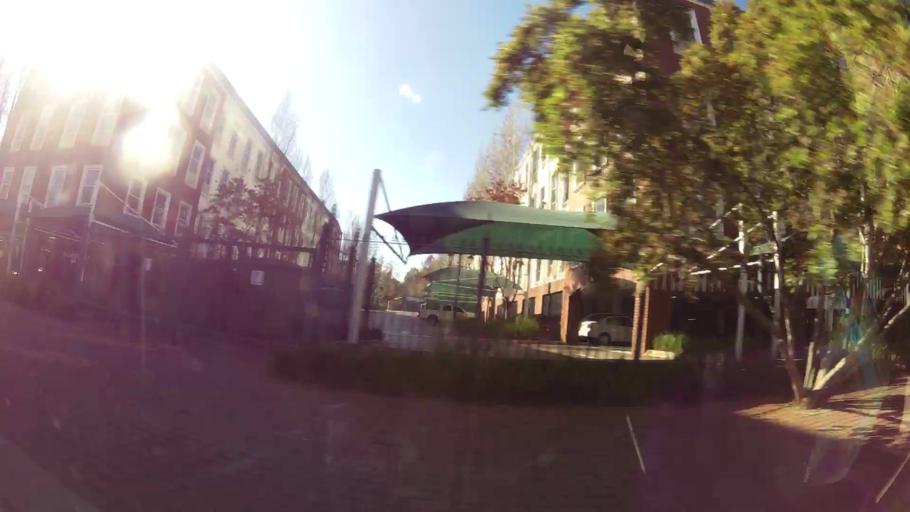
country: ZA
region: Gauteng
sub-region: City of Tshwane Metropolitan Municipality
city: Centurion
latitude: -25.8577
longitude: 28.2176
